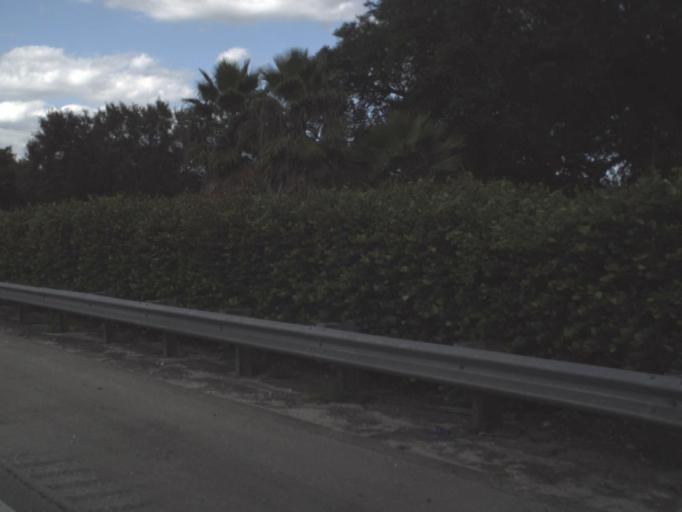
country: US
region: Florida
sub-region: Broward County
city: Pembroke Pines
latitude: 26.0207
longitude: -80.2128
